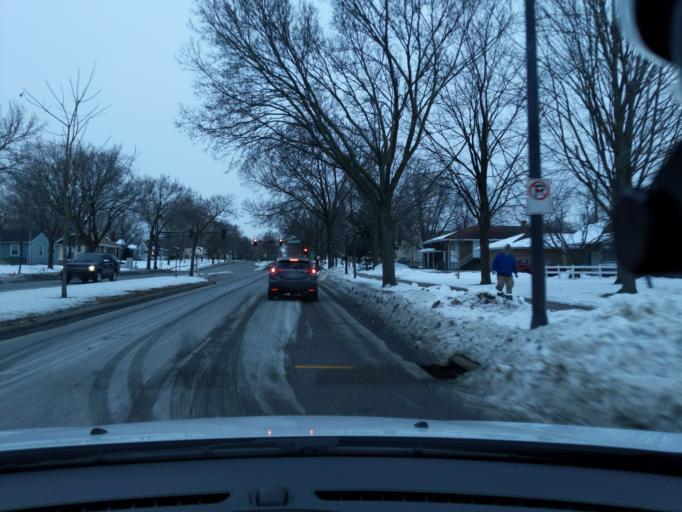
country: US
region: Minnesota
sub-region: Ramsey County
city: Falcon Heights
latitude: 44.9639
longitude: -93.1467
